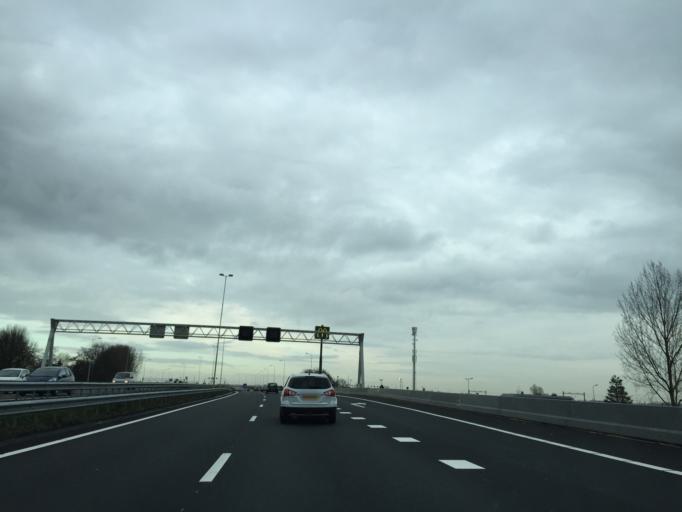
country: NL
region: South Holland
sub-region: Gemeente Waddinxveen
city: Waddinxveen
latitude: 51.9983
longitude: 4.6486
